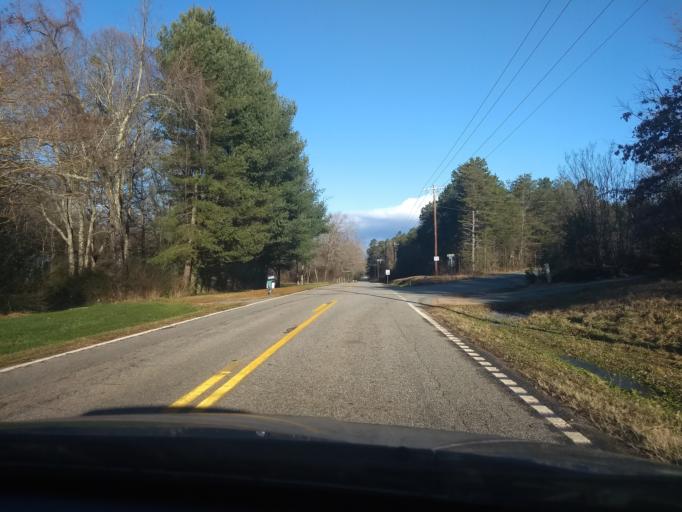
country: US
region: South Carolina
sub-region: Greenville County
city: Greer
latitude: 35.0057
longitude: -82.2155
